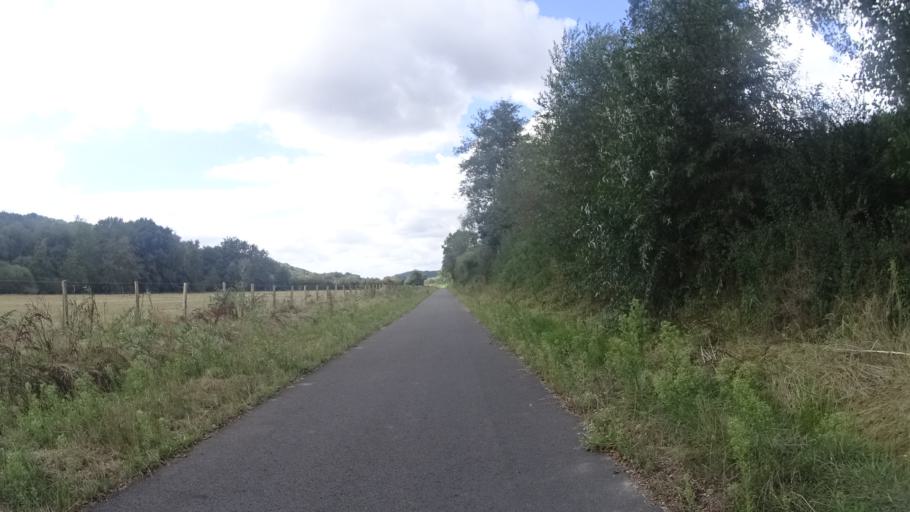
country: FR
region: Bourgogne
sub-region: Departement de Saone-et-Loire
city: Couches
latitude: 46.8071
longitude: 4.5756
